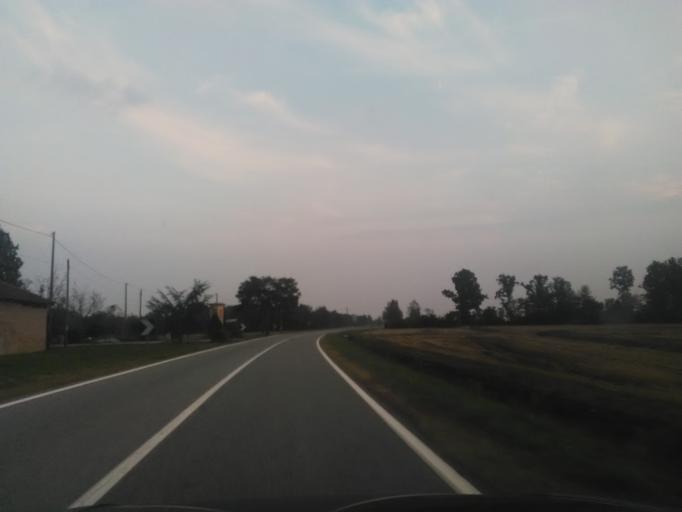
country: IT
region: Piedmont
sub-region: Provincia di Vercelli
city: Rovasenda
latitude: 45.5532
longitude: 8.3010
